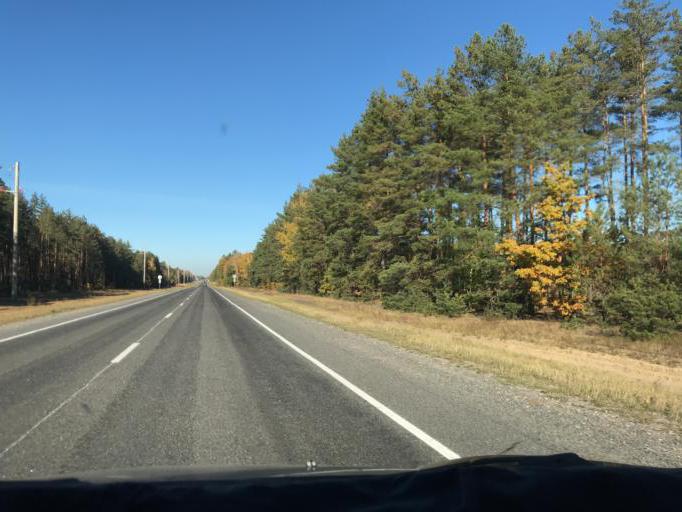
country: BY
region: Gomel
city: Yel'sk
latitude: 51.8929
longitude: 29.2425
